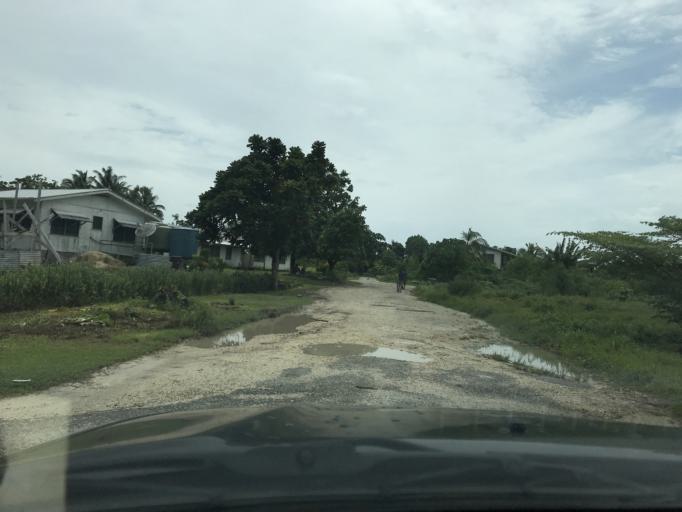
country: SB
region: Western Province
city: Gizo
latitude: -8.3296
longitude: 157.2508
